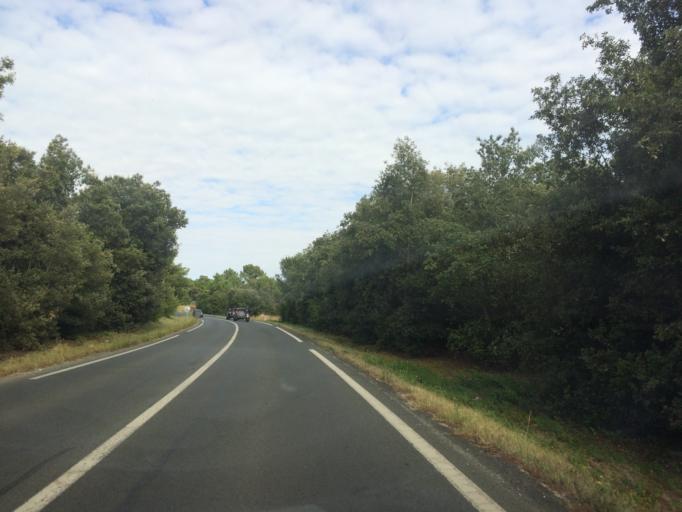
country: FR
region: Poitou-Charentes
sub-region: Departement de la Charente-Maritime
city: La Flotte
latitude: 46.1787
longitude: -1.3301
